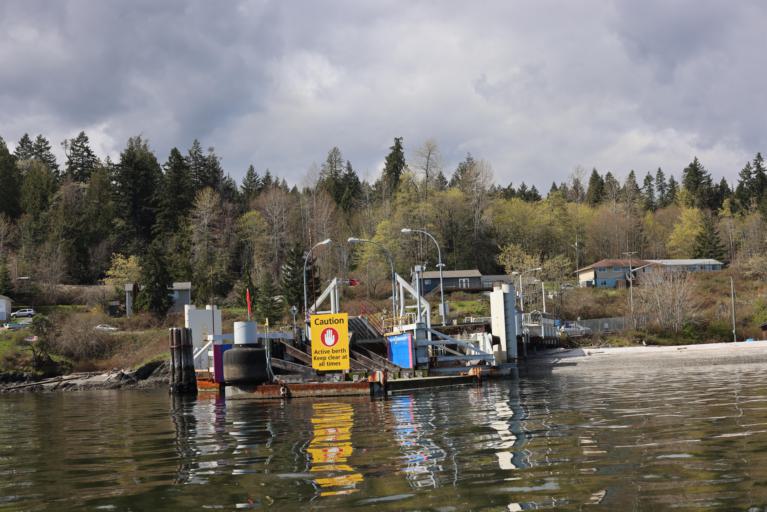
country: CA
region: British Columbia
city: North Saanich
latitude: 48.6141
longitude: -123.5167
